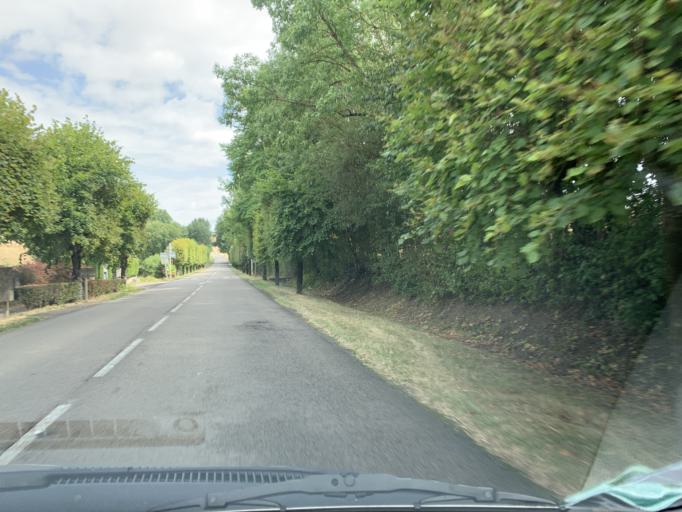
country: FR
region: Bourgogne
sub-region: Departement de la Nievre
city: Varzy
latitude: 47.3600
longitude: 3.3925
